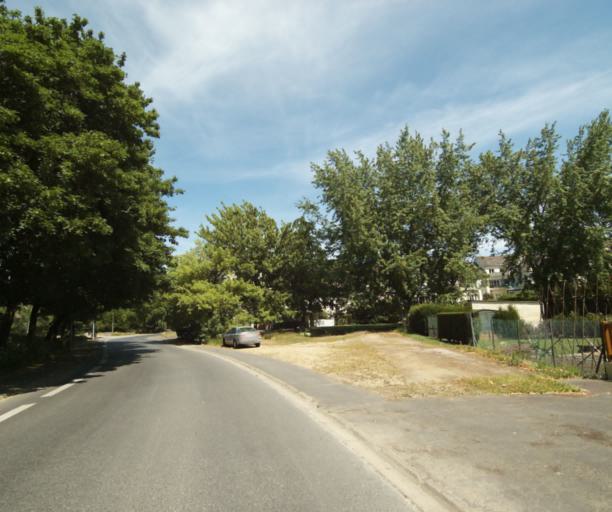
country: FR
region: Champagne-Ardenne
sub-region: Departement des Ardennes
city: Charleville-Mezieres
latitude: 49.7579
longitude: 4.7115
